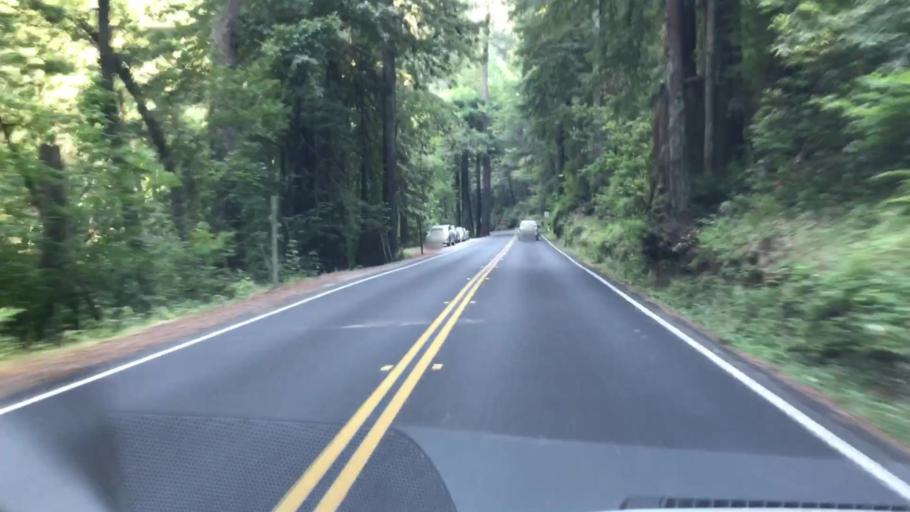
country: US
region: California
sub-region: Marin County
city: Lagunitas-Forest Knolls
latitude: 38.0070
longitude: -122.7115
